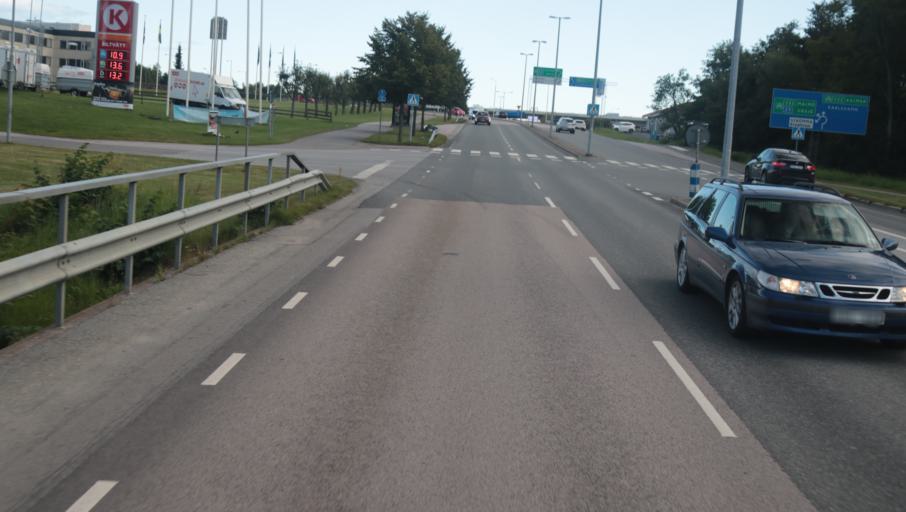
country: SE
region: Blekinge
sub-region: Karlshamns Kommun
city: Karlshamn
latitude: 56.1912
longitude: 14.8448
